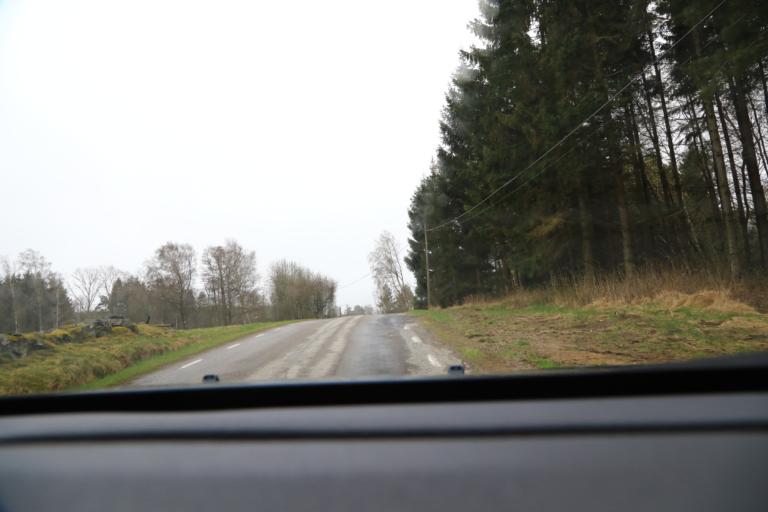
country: SE
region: Halland
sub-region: Kungsbacka Kommun
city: Frillesas
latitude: 57.2755
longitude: 12.2013
